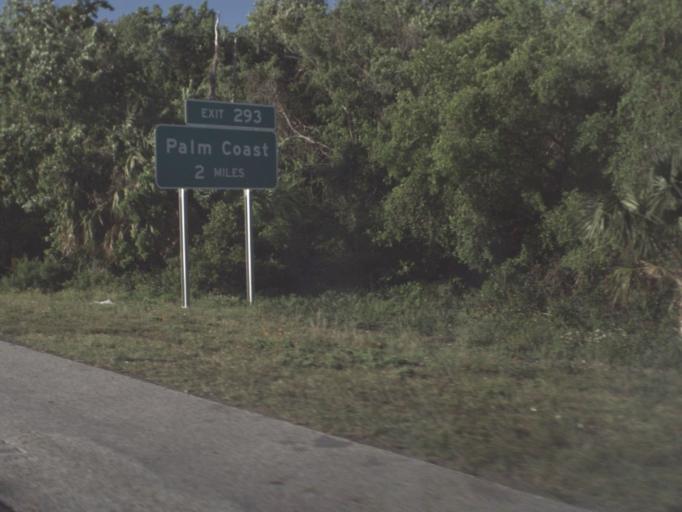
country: US
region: Florida
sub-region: Flagler County
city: Palm Coast
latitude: 29.5738
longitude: -81.2315
